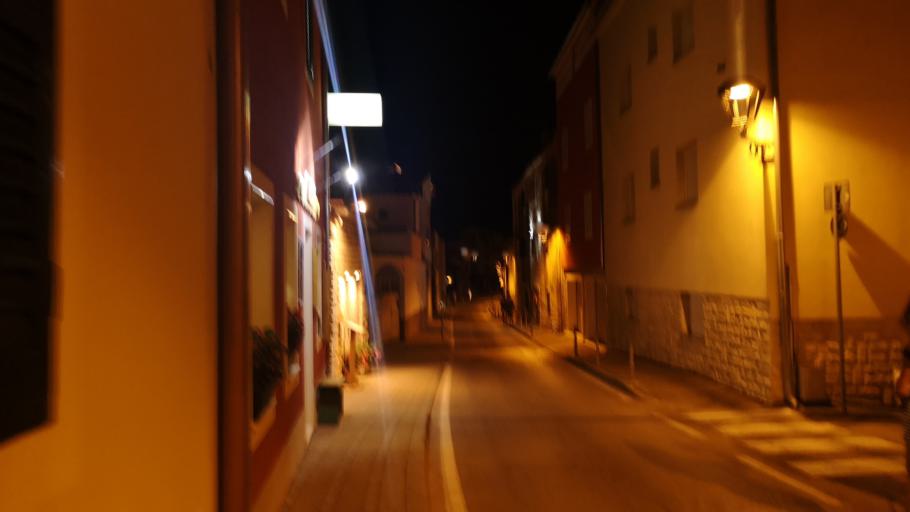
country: HR
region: Sibensko-Kniniska
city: Vodice
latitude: 43.7584
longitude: 15.7734
